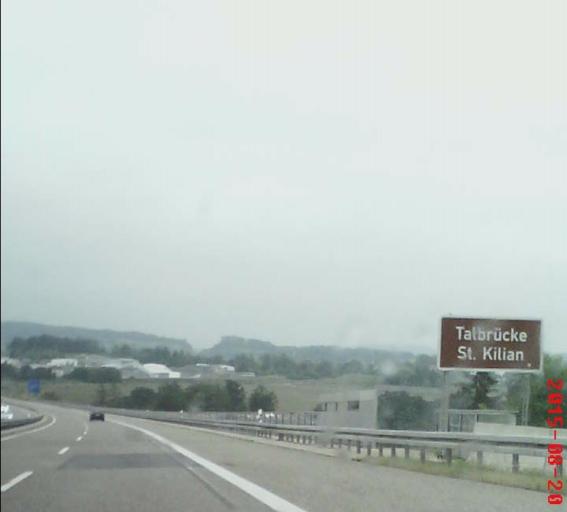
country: DE
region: Thuringia
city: Sankt Kilian
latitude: 50.5258
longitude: 10.7491
